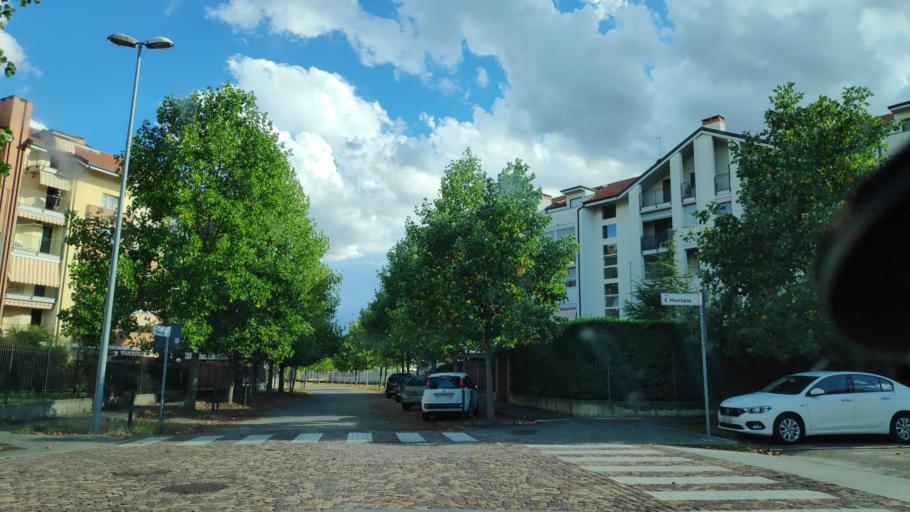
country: IT
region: Piedmont
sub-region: Provincia di Torino
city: La Loggia
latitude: 44.9524
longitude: 7.6727
